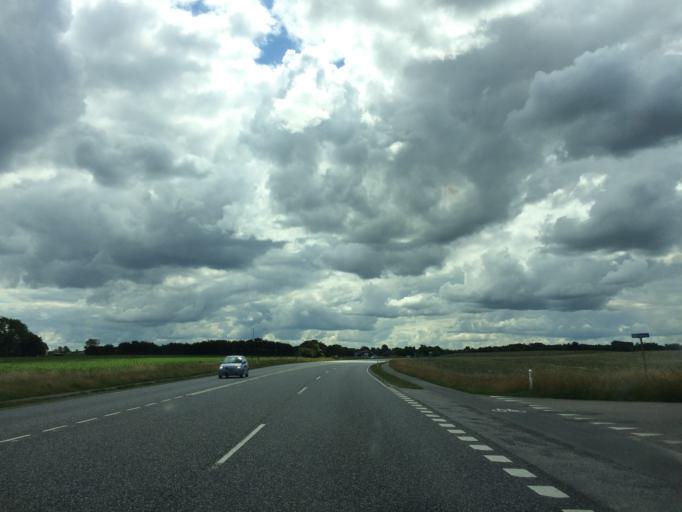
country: DK
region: Central Jutland
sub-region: Viborg Kommune
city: Viborg
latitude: 56.5444
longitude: 9.4755
